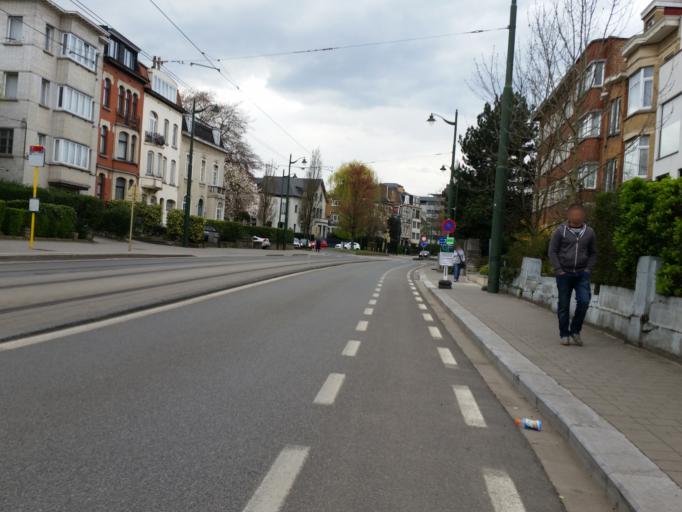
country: BE
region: Flanders
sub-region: Provincie Vlaams-Brabant
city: Dilbeek
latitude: 50.8619
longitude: 4.3018
